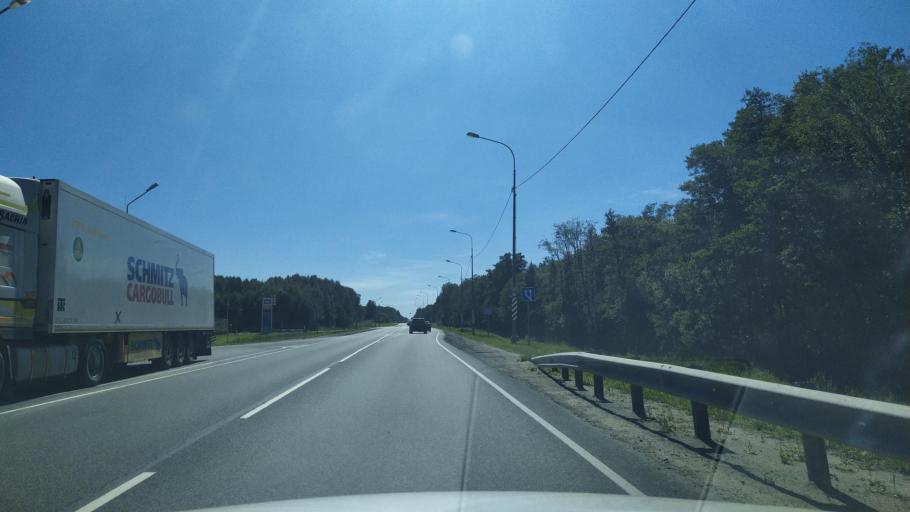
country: RU
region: Pskov
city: Pskov
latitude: 57.7835
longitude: 28.4064
